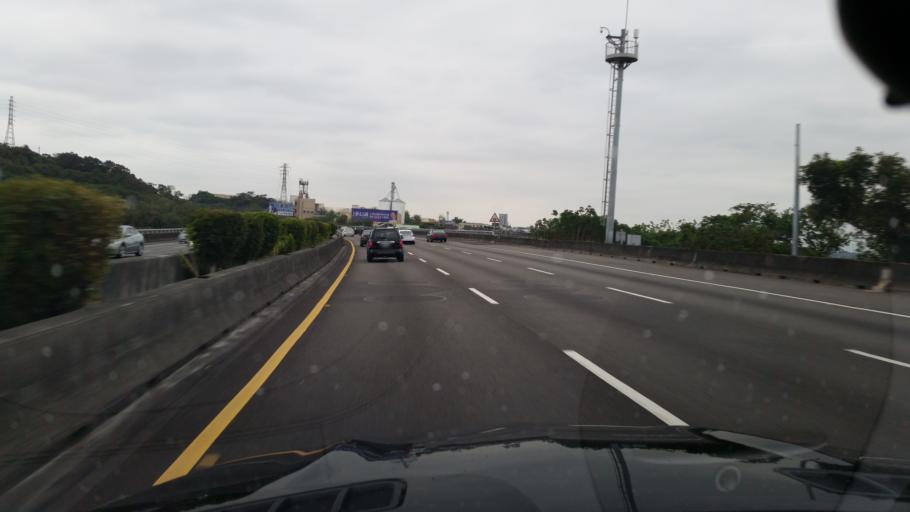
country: TW
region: Taiwan
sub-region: Miaoli
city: Miaoli
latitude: 24.6690
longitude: 120.8860
